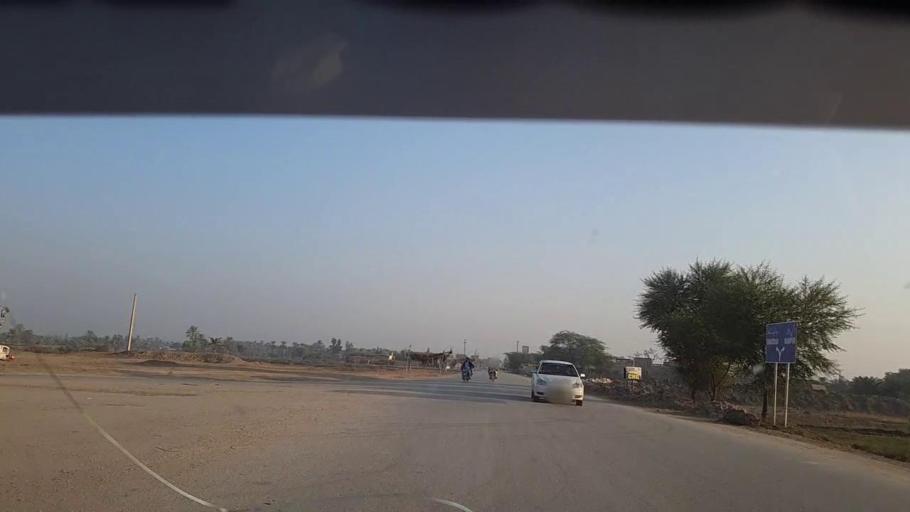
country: PK
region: Sindh
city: Ranipur
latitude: 27.2659
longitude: 68.5217
